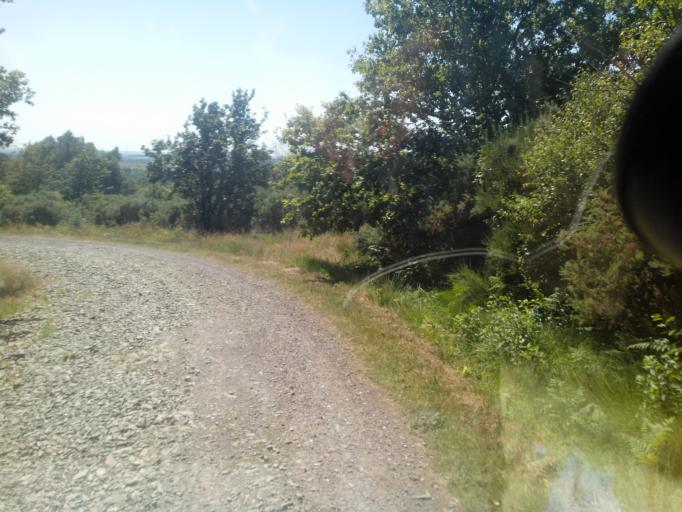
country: FR
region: Brittany
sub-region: Departement du Morbihan
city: Campeneac
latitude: 47.9816
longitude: -2.2622
